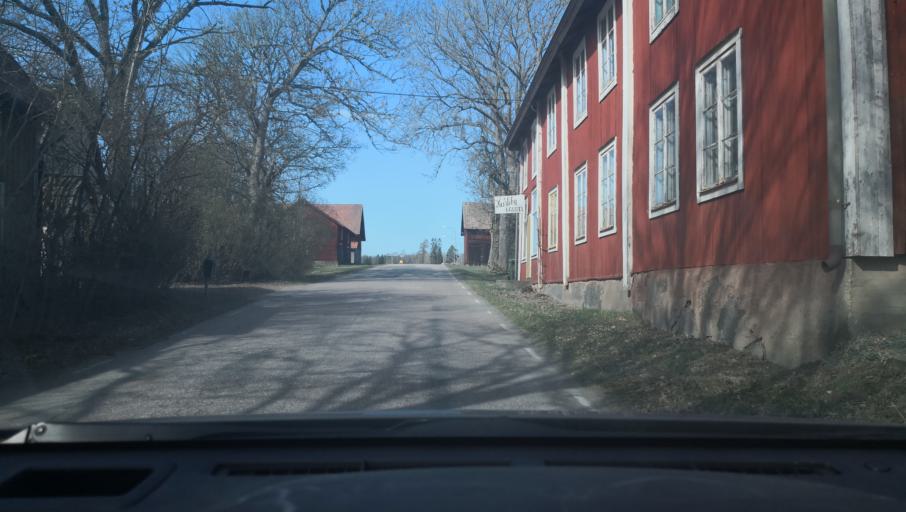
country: SE
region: Uppsala
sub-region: Enkopings Kommun
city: Irsta
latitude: 59.7731
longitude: 16.8840
